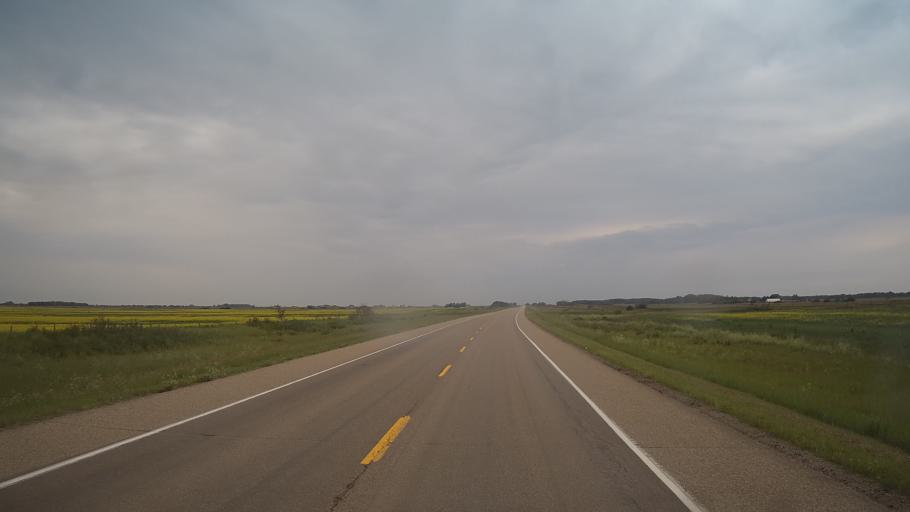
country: CA
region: Saskatchewan
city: Langham
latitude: 52.1277
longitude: -107.2491
